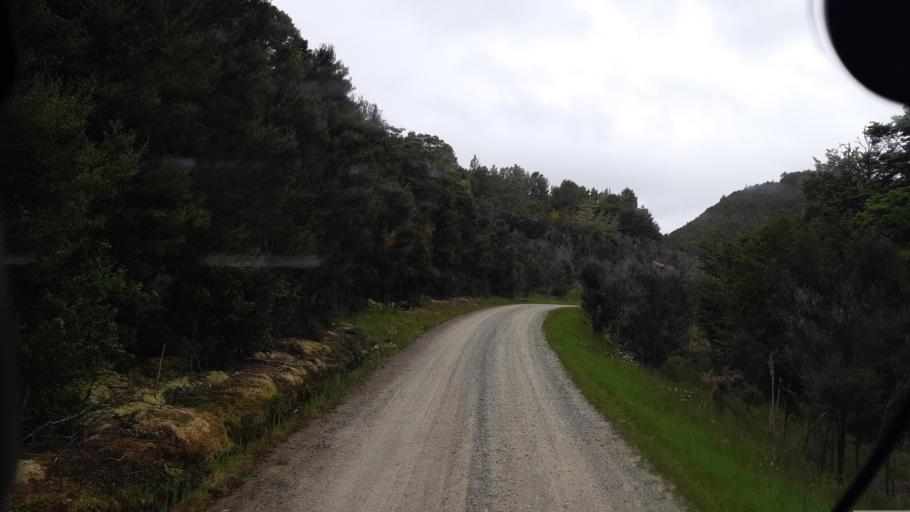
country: NZ
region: West Coast
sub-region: Buller District
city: Westport
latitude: -42.2930
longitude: 171.8233
